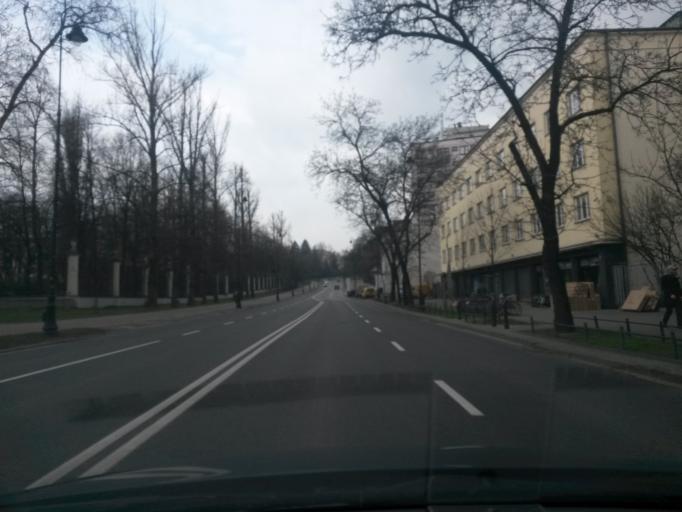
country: PL
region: Masovian Voivodeship
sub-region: Warszawa
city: Mokotow
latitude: 52.2091
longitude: 21.0291
